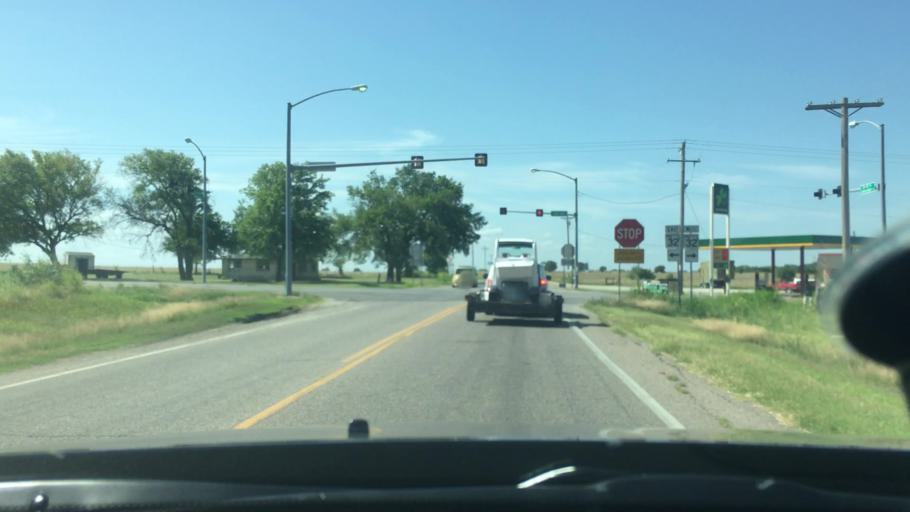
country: US
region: Oklahoma
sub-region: Marshall County
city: Kingston
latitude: 33.9988
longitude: -96.7611
